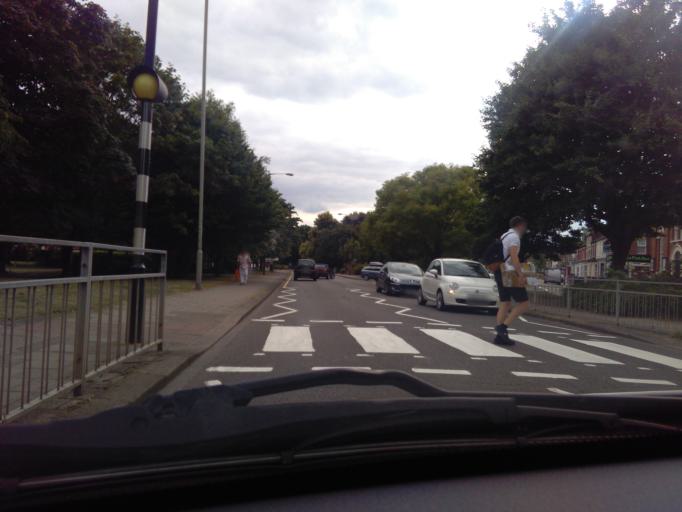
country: GB
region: England
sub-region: Bedford
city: Bedford
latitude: 52.1431
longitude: -0.4721
